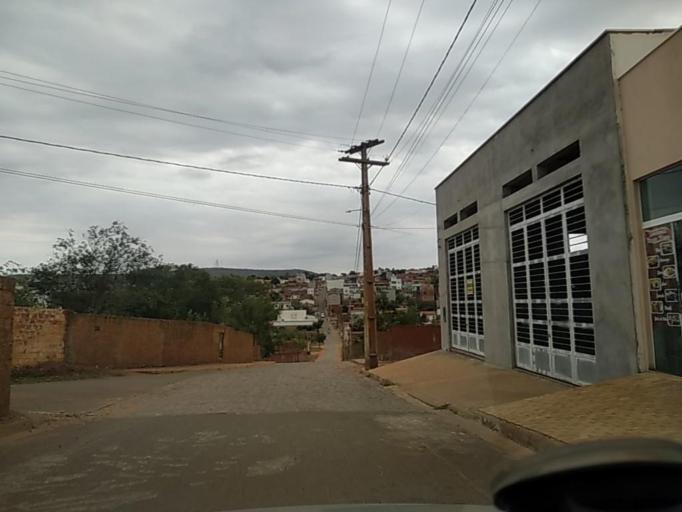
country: BR
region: Bahia
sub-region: Caetite
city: Caetite
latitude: -14.0530
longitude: -42.4770
